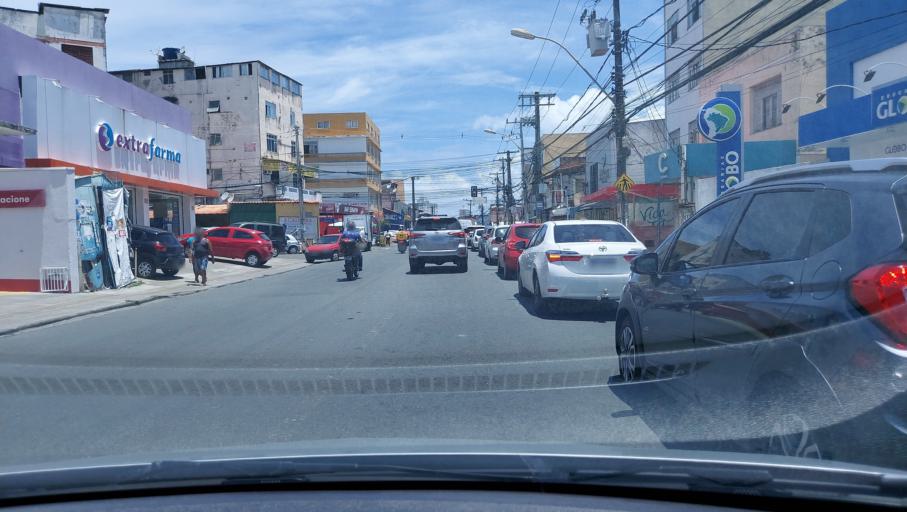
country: BR
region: Bahia
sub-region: Salvador
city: Salvador
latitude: -12.9883
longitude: -38.4797
